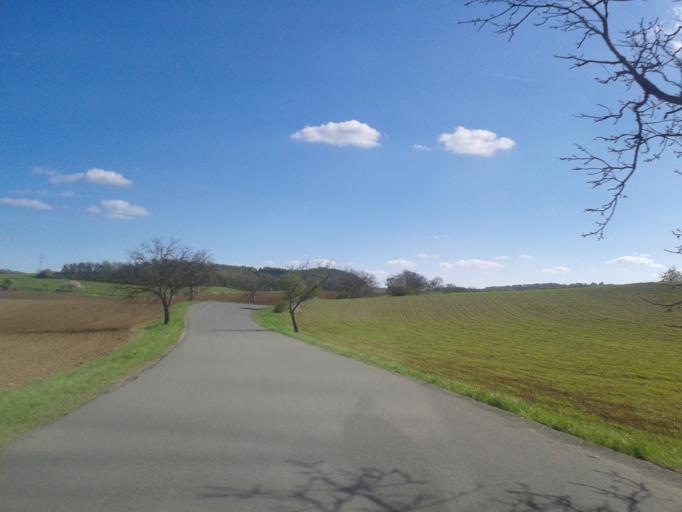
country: CZ
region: Central Bohemia
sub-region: Okres Beroun
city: Beroun
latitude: 49.9333
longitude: 14.0732
